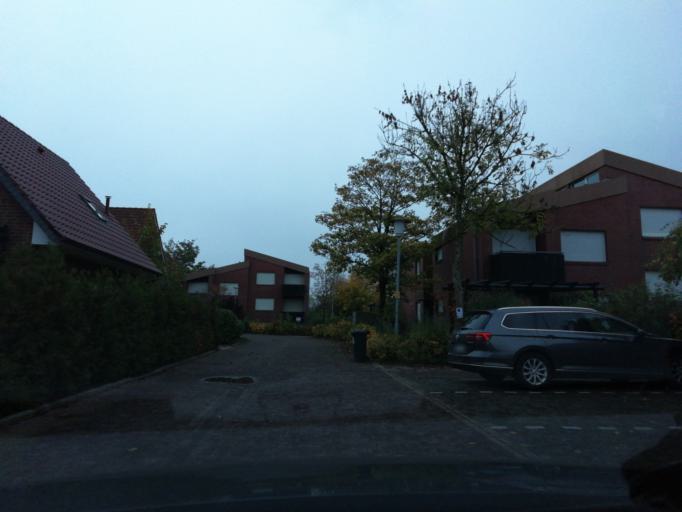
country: DE
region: Lower Saxony
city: Schillig
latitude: 53.6357
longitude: 8.0338
